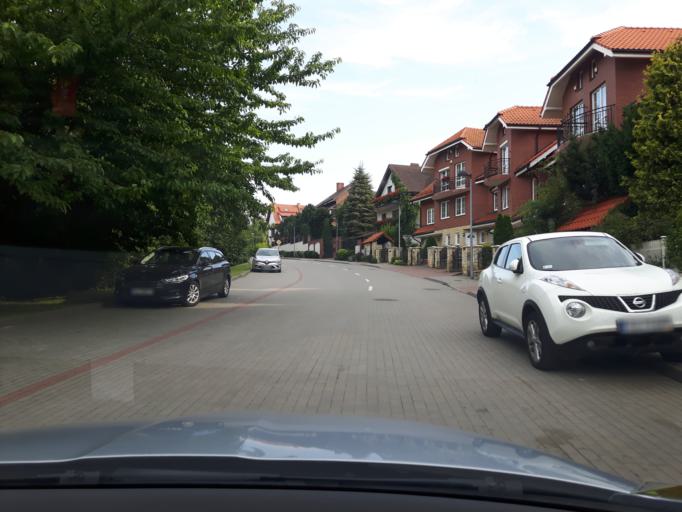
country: PL
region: Pomeranian Voivodeship
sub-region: Gdynia
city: Gdynia
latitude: 54.5035
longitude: 18.5466
